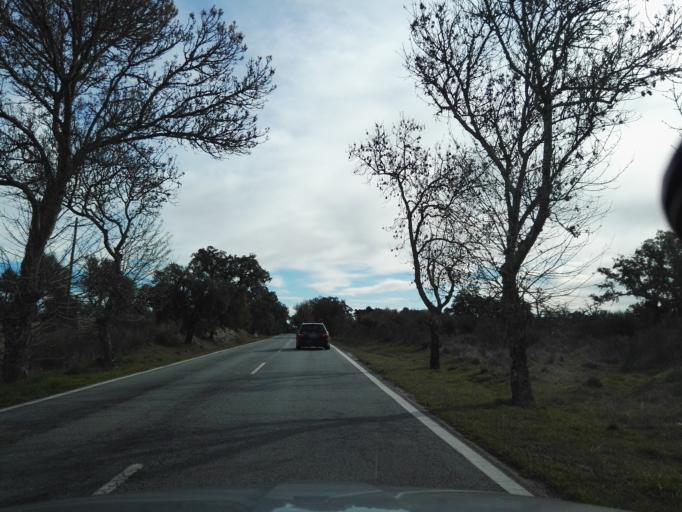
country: PT
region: Portalegre
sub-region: Nisa
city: Nisa
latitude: 39.5000
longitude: -7.6817
